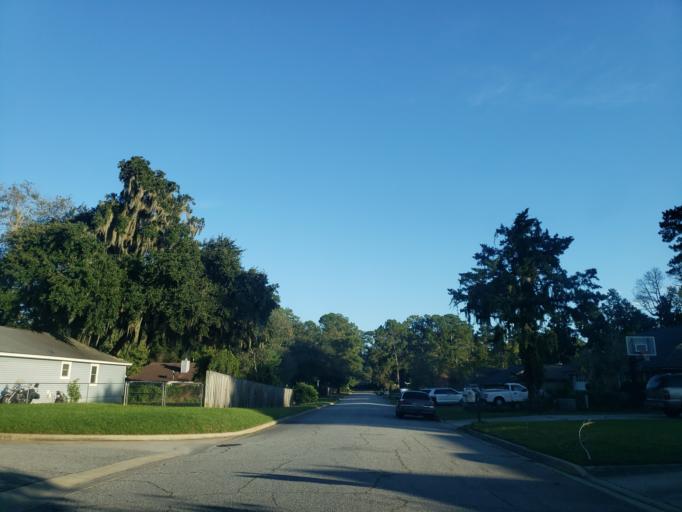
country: US
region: Georgia
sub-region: Chatham County
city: Isle of Hope
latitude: 31.9966
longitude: -81.0655
